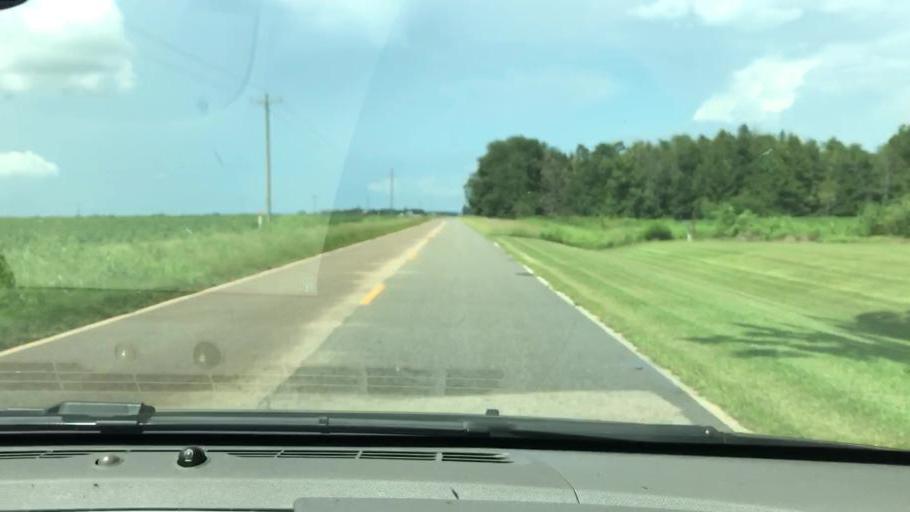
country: US
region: Georgia
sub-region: Seminole County
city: Donalsonville
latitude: 31.0958
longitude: -84.9962
